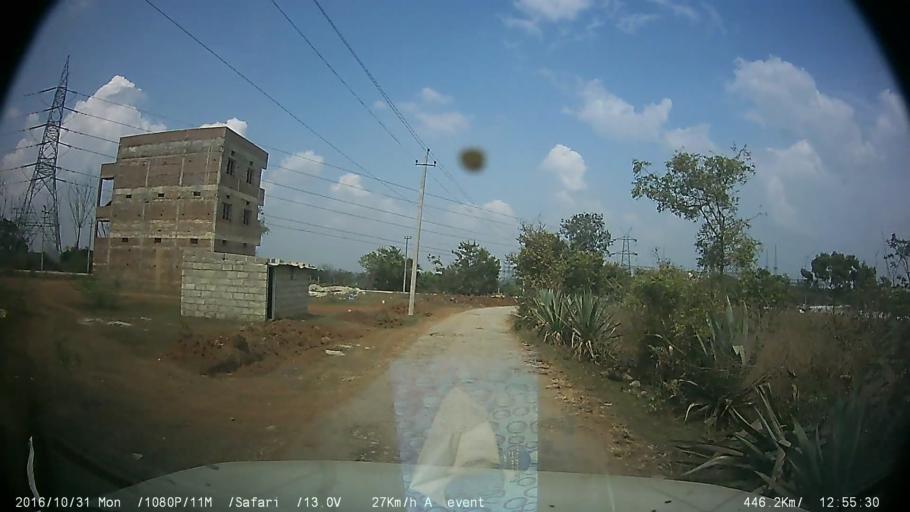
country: IN
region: Karnataka
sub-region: Mysore
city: Mysore
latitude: 12.3663
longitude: 76.5604
